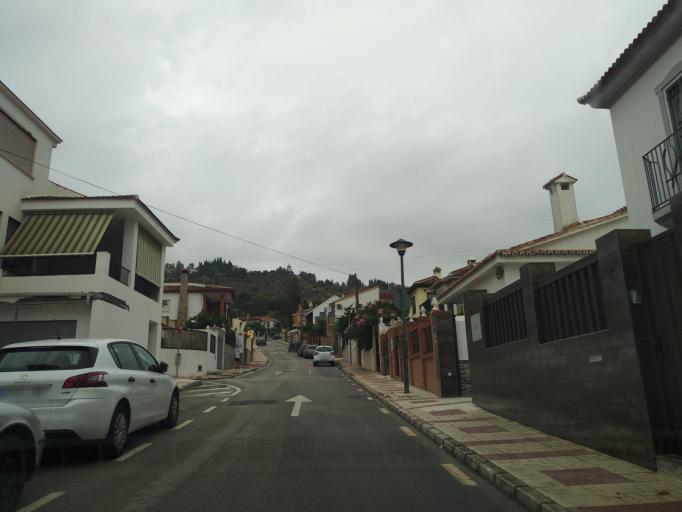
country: ES
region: Andalusia
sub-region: Provincia de Malaga
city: Malaga
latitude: 36.7399
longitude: -4.4787
